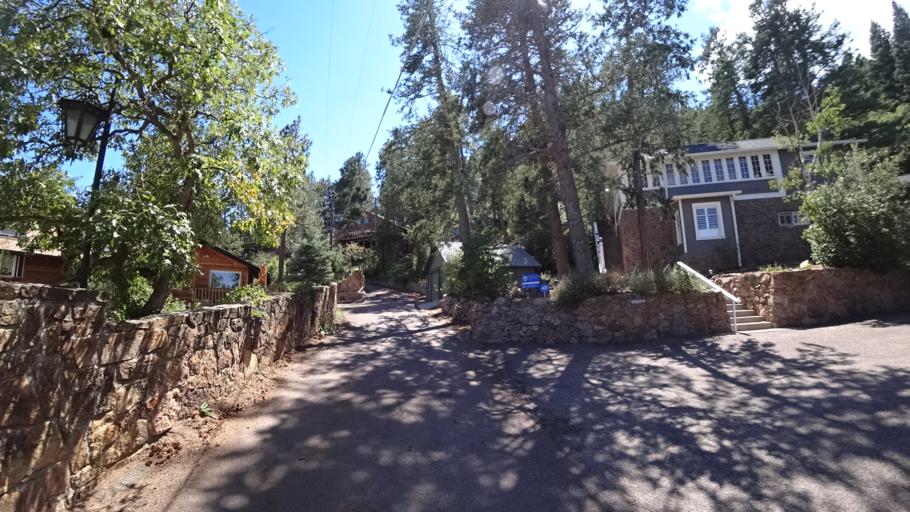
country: US
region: Colorado
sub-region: El Paso County
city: Colorado Springs
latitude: 38.7776
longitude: -104.8613
